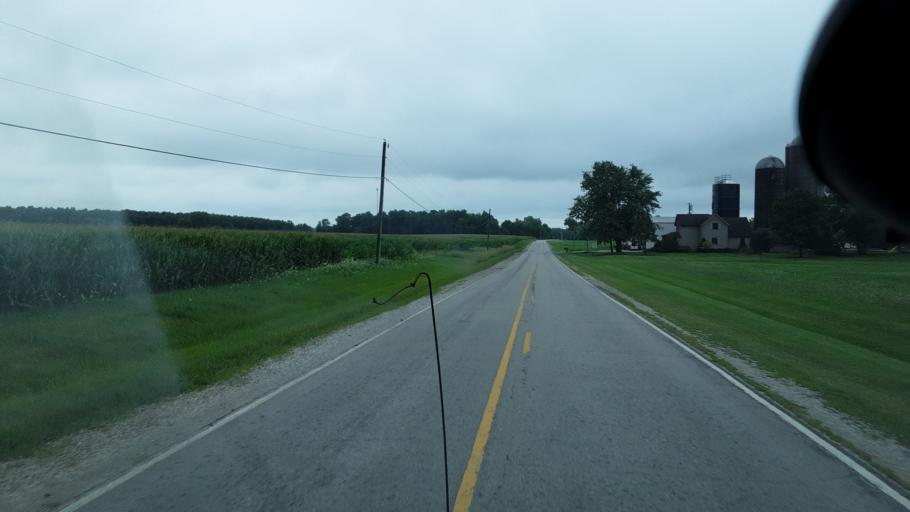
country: US
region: Indiana
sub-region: Wells County
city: Bluffton
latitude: 40.7192
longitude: -85.0890
